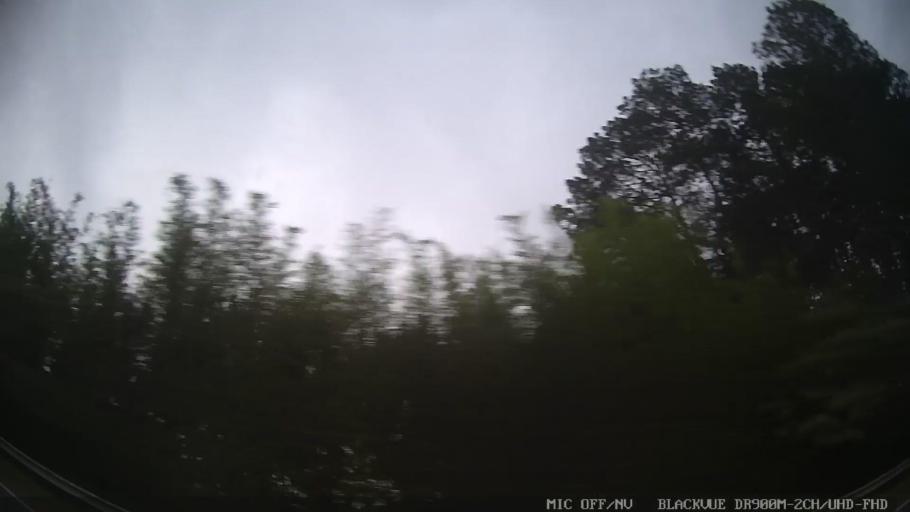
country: BR
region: Sao Paulo
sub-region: Itatiba
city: Itatiba
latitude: -22.9149
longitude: -46.7859
